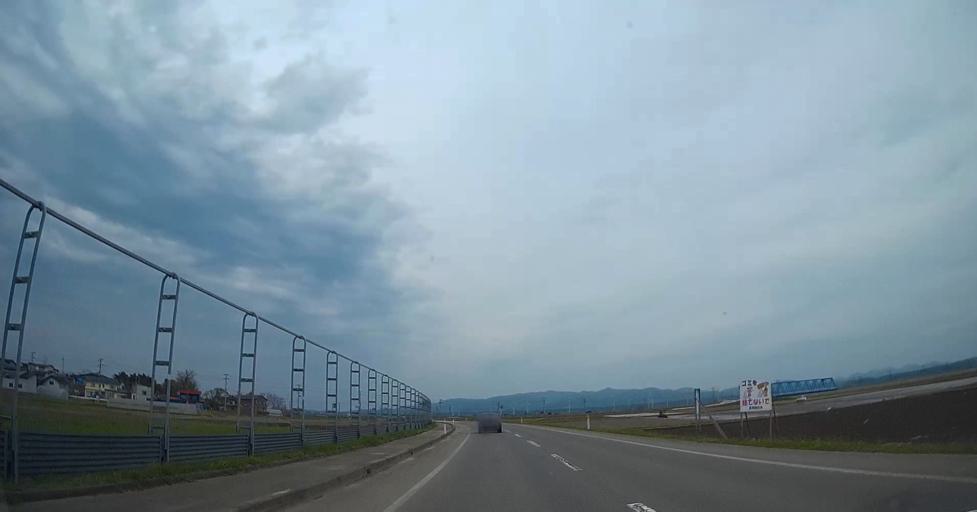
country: JP
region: Aomori
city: Shimokizukuri
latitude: 40.9827
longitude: 140.3765
